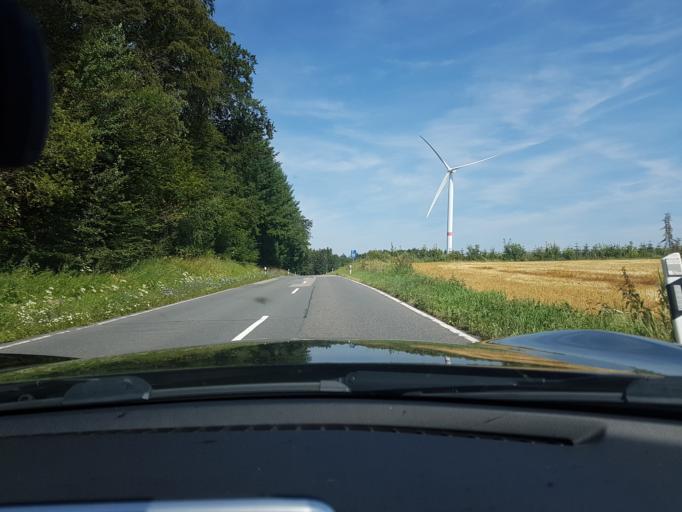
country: DE
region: Baden-Wuerttemberg
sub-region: Karlsruhe Region
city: Limbach
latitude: 49.4517
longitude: 9.2716
